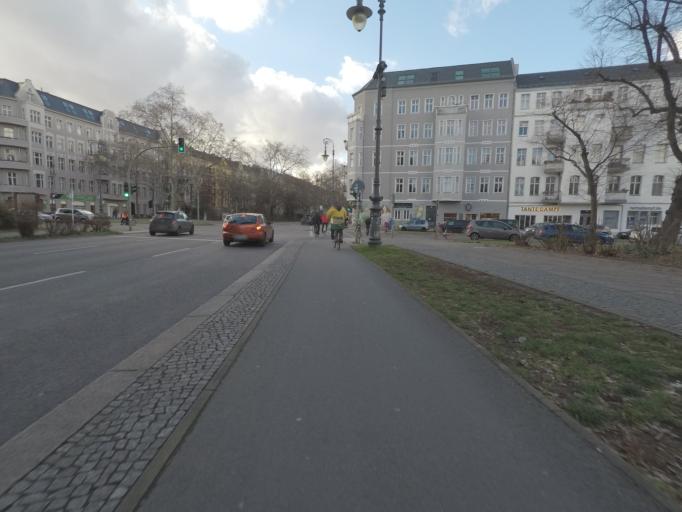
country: DE
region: Berlin
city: Bezirk Kreuzberg
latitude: 52.4896
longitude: 13.4063
